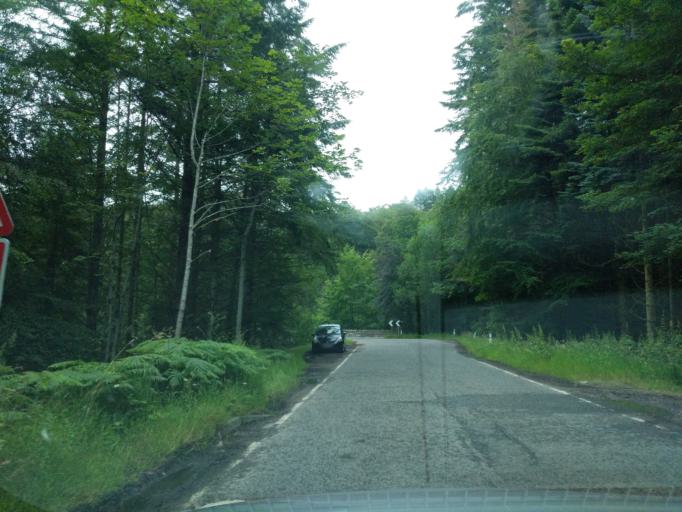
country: GB
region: Scotland
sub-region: Moray
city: Forres
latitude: 57.5267
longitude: -3.6666
